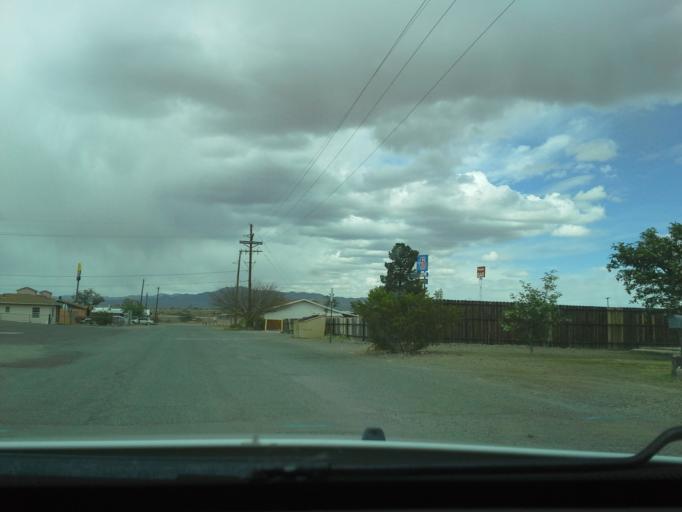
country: US
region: New Mexico
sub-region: Hidalgo County
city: Lordsburg
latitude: 32.3412
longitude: -108.7159
